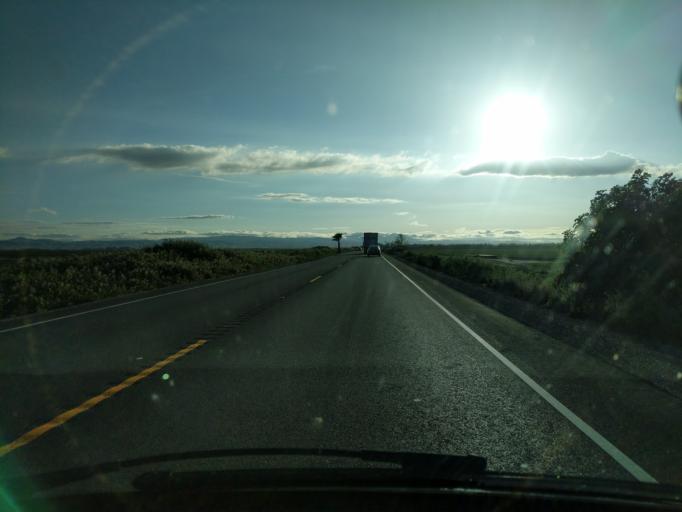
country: US
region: California
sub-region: Contra Costa County
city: Discovery Bay
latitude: 37.8913
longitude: -121.4984
